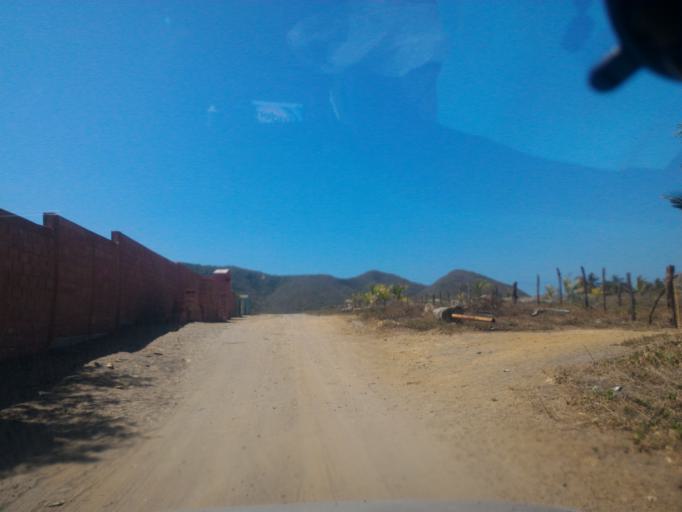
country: MX
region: Michoacan
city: Coahuayana Viejo
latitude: 18.5924
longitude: -103.6915
